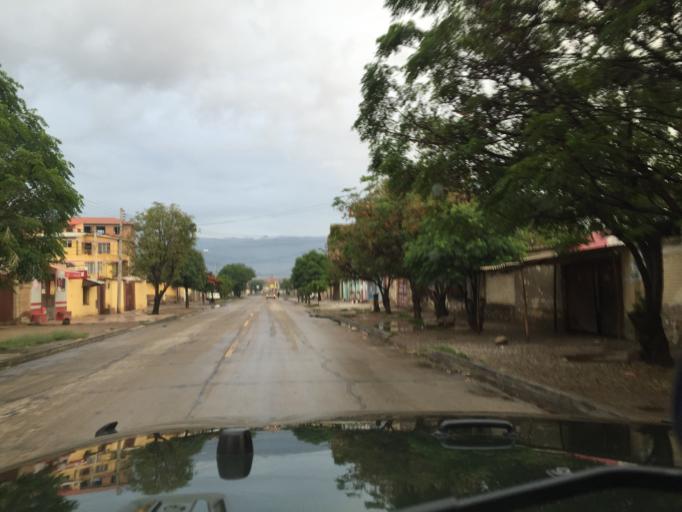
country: BO
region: Cochabamba
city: Cochabamba
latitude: -17.4185
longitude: -66.1673
